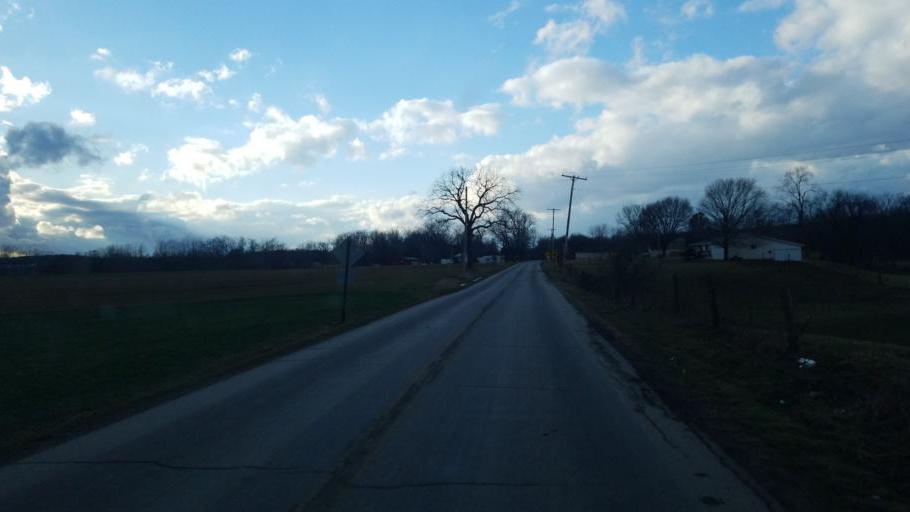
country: US
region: Ohio
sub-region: Richland County
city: Lexington
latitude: 40.6198
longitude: -82.6093
